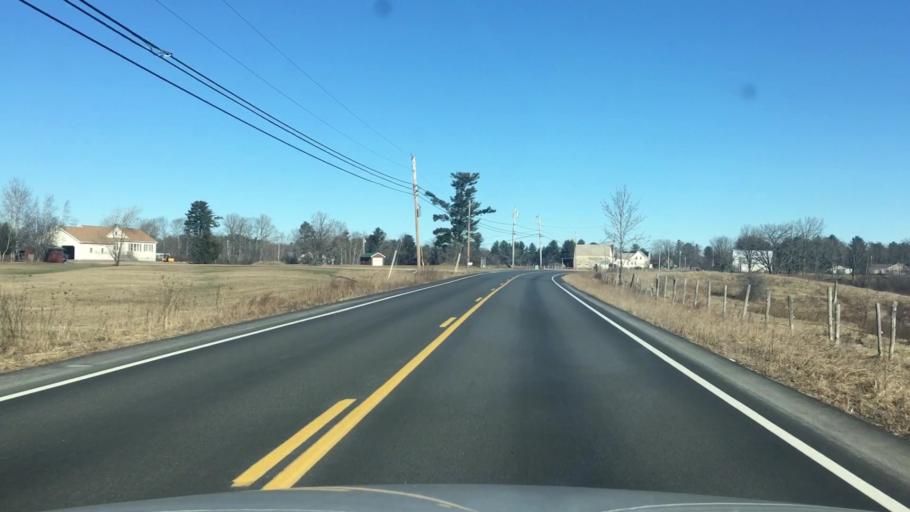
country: US
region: Maine
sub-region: Kennebec County
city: Benton
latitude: 44.5981
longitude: -69.5435
